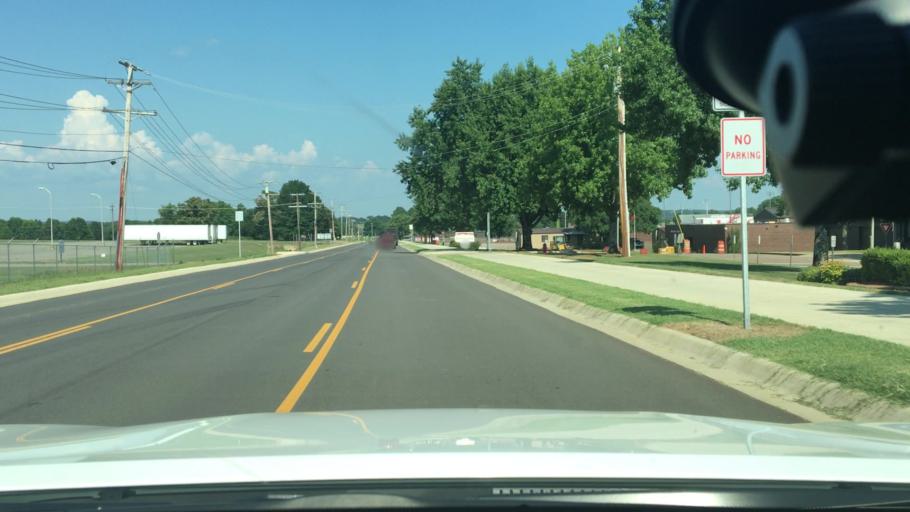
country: US
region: Arkansas
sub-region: Johnson County
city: Clarksville
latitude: 35.4619
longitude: -93.4910
